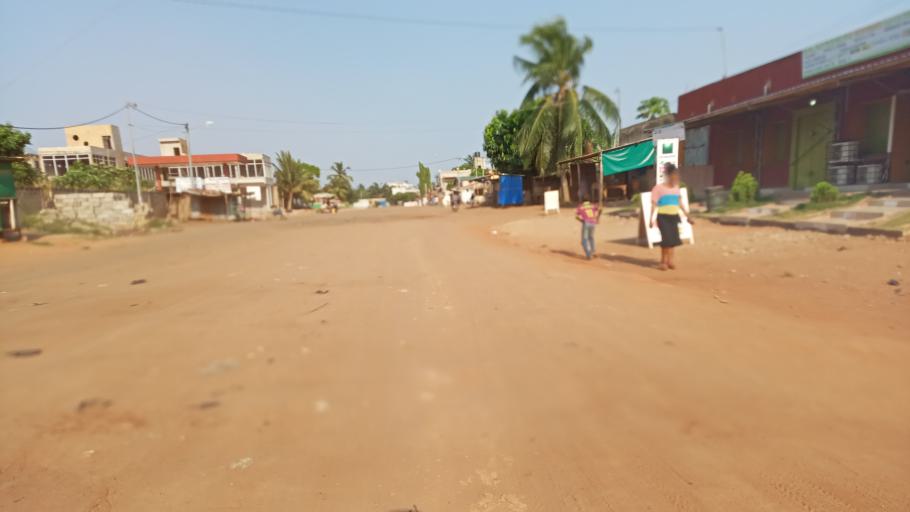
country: TG
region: Maritime
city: Lome
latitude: 6.1804
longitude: 1.1536
